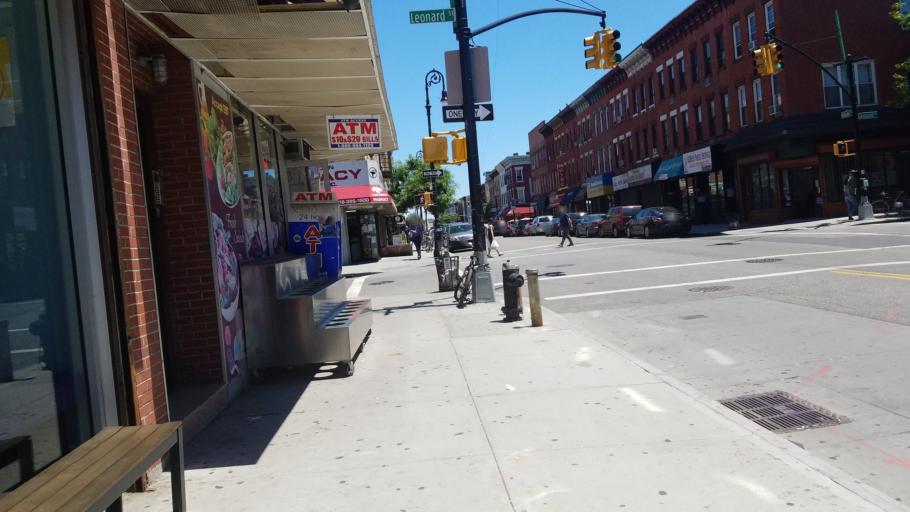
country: US
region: New York
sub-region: Queens County
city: Long Island City
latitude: 40.7240
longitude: -73.9502
